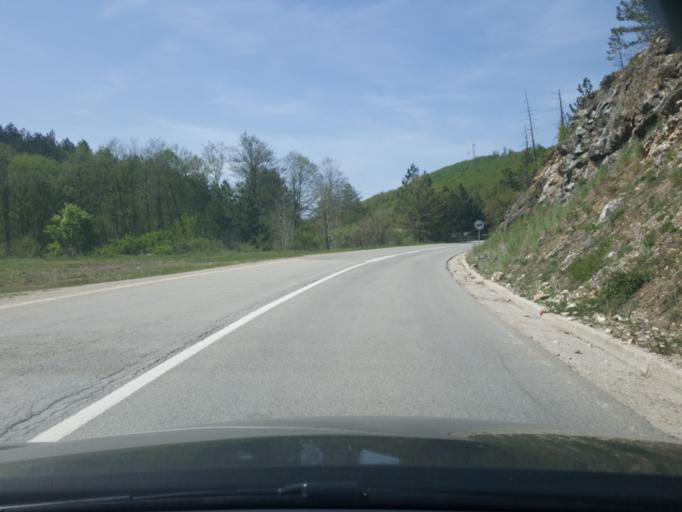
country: RS
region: Central Serbia
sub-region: Zlatiborski Okrug
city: Cajetina
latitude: 43.7919
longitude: 19.6576
